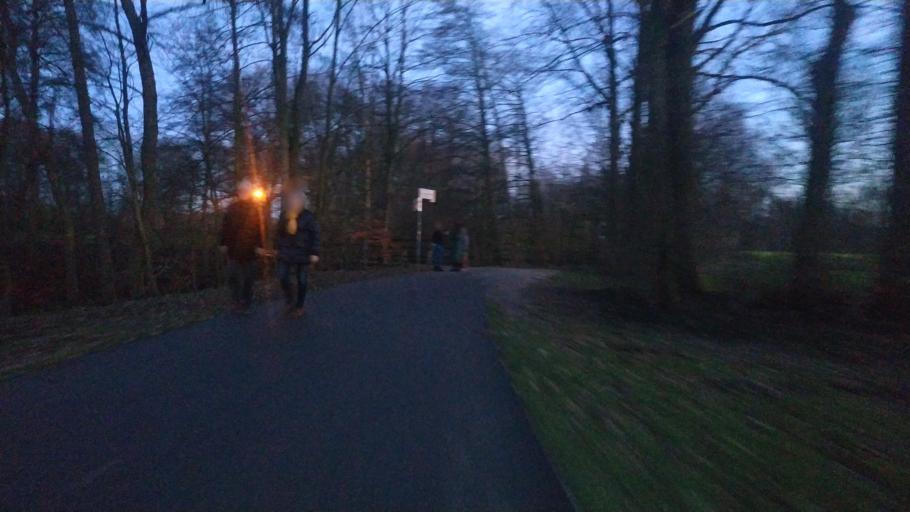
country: DE
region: North Rhine-Westphalia
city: Ibbenburen
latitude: 52.2639
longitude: 7.7329
